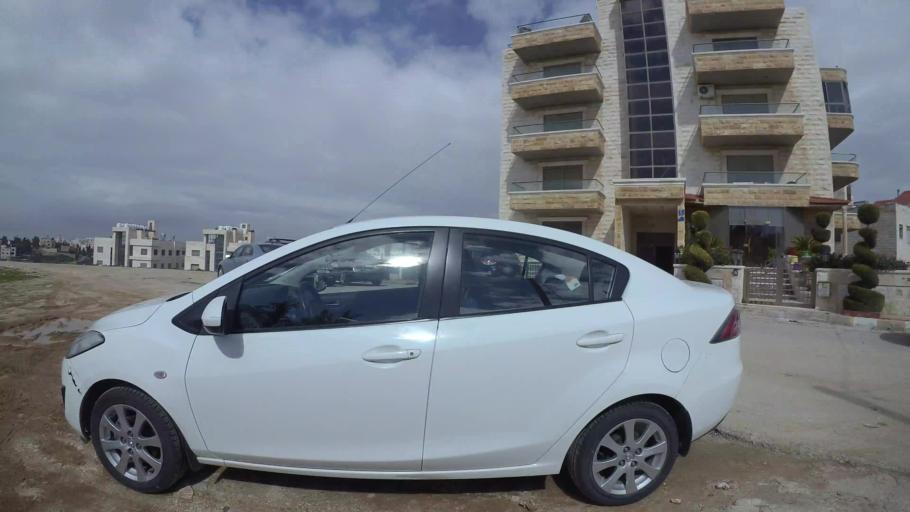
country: JO
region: Amman
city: Al Jubayhah
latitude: 31.9989
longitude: 35.8345
